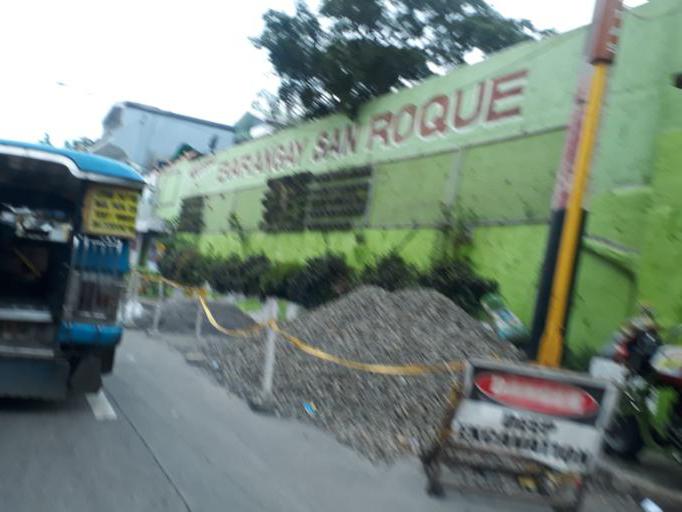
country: PH
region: Calabarzon
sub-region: Province of Rizal
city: Malabon
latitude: 14.6710
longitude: 120.9403
